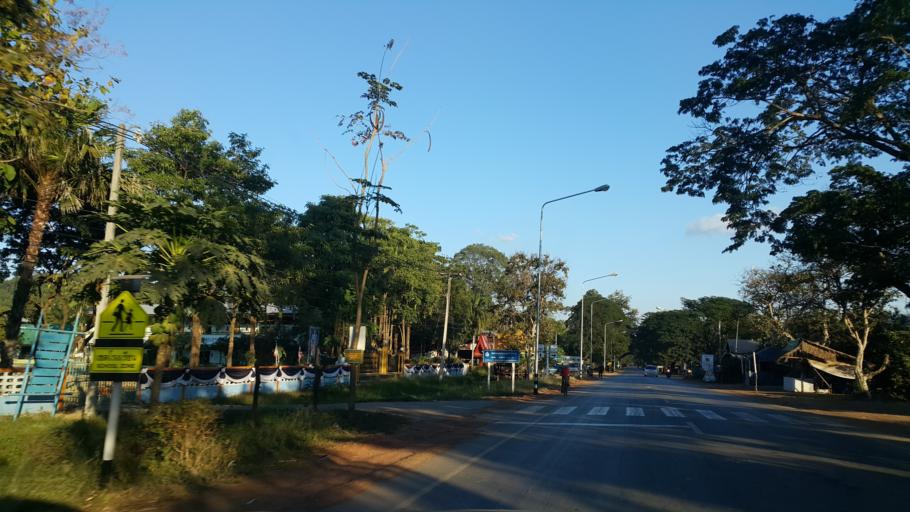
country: TH
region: Sukhothai
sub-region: Amphoe Si Satchanalai
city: Si Satchanalai
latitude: 17.5524
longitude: 99.8778
